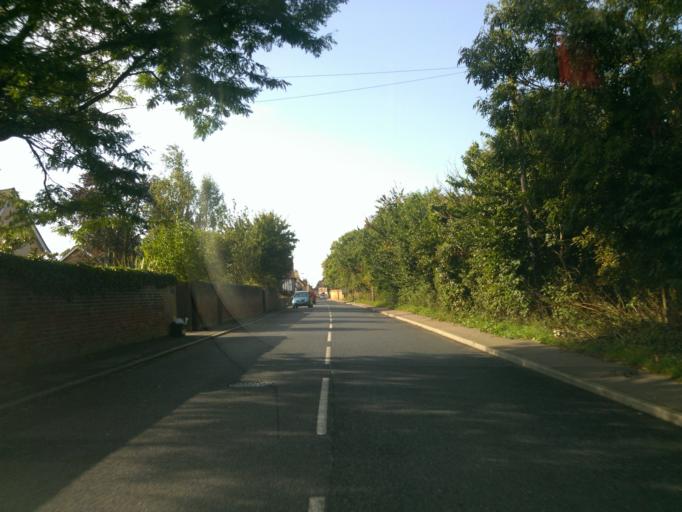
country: GB
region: England
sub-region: Essex
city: Saint Osyth
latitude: 51.8024
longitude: 1.0783
